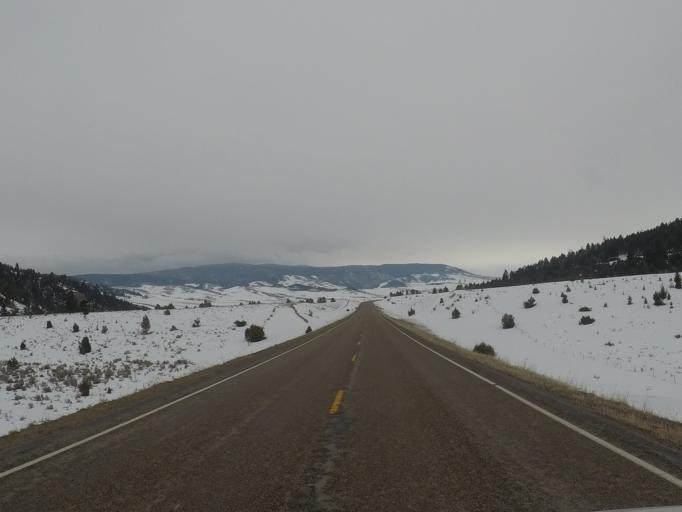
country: US
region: Montana
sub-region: Meagher County
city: White Sulphur Springs
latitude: 46.6126
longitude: -110.8435
